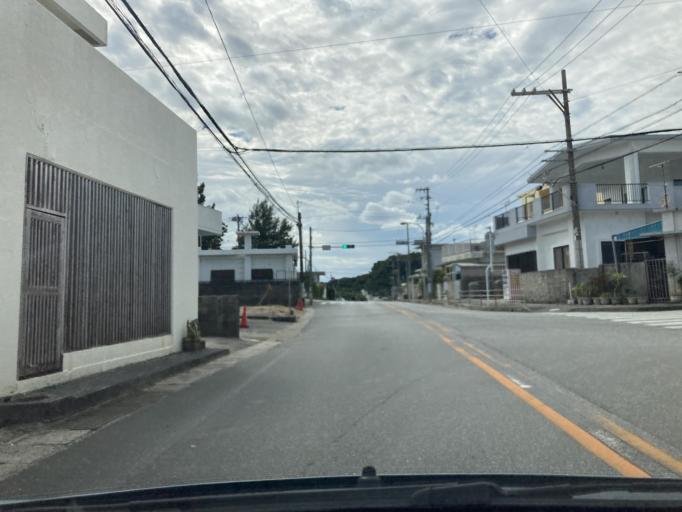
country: JP
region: Okinawa
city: Ishikawa
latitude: 26.4337
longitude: 127.7780
